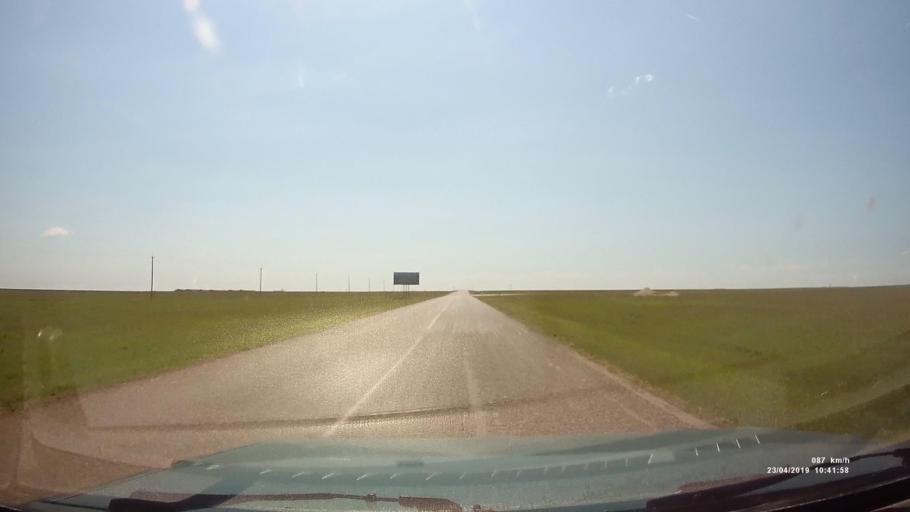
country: RU
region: Kalmykiya
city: Yashalta
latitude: 46.4882
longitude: 42.6404
